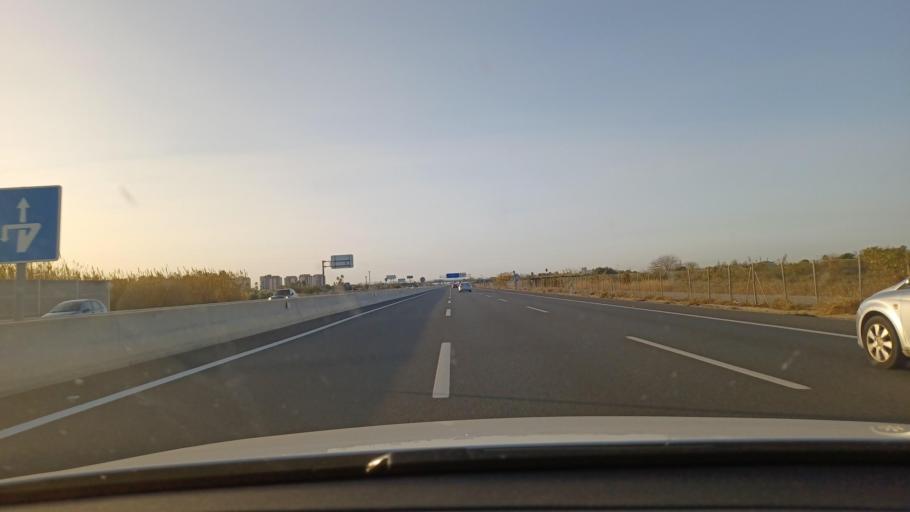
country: ES
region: Valencia
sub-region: Provincia de Valencia
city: Puig
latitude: 39.5753
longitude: -0.2951
